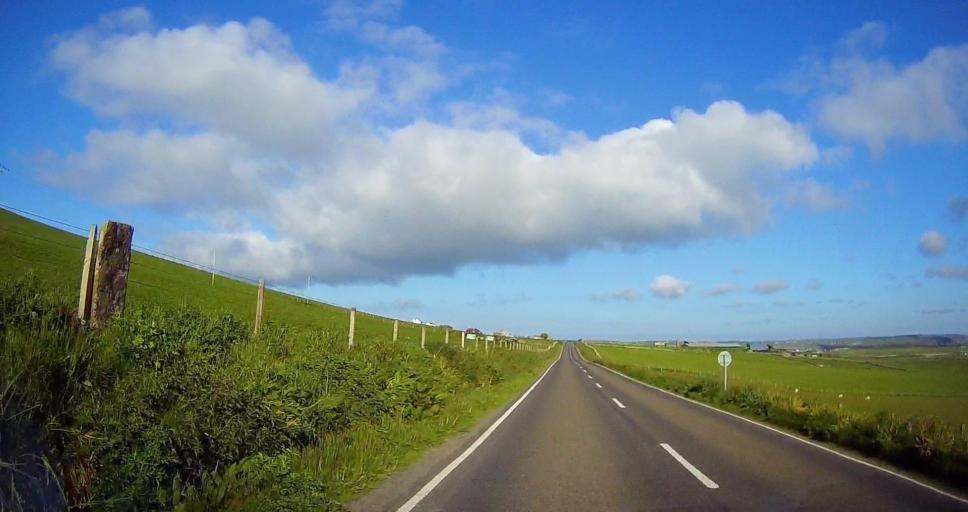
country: GB
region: Scotland
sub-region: Orkney Islands
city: Orkney
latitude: 58.9803
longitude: -3.0325
